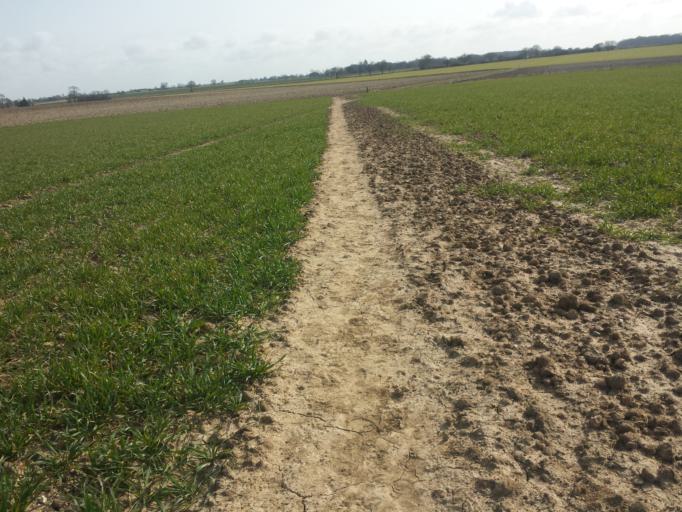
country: GB
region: England
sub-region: Essex
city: Mistley
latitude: 51.9084
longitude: 1.1513
